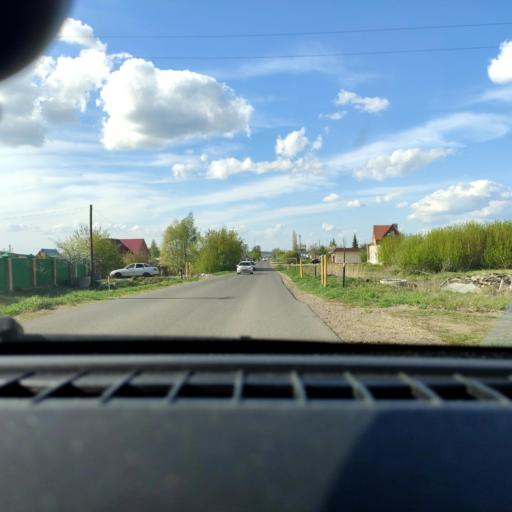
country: RU
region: Samara
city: Zhigulevsk
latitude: 53.3509
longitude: 49.4757
